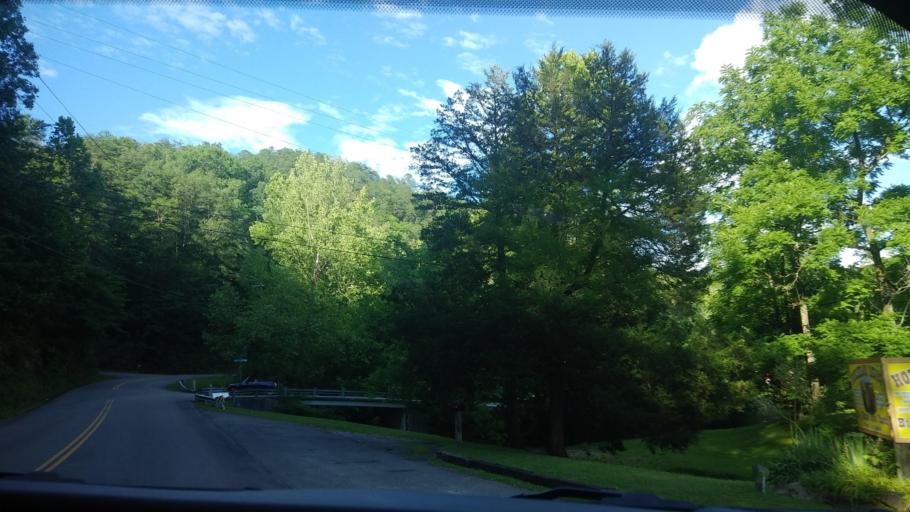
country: US
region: Tennessee
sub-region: Sevier County
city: Pigeon Forge
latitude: 35.7637
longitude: -83.5696
